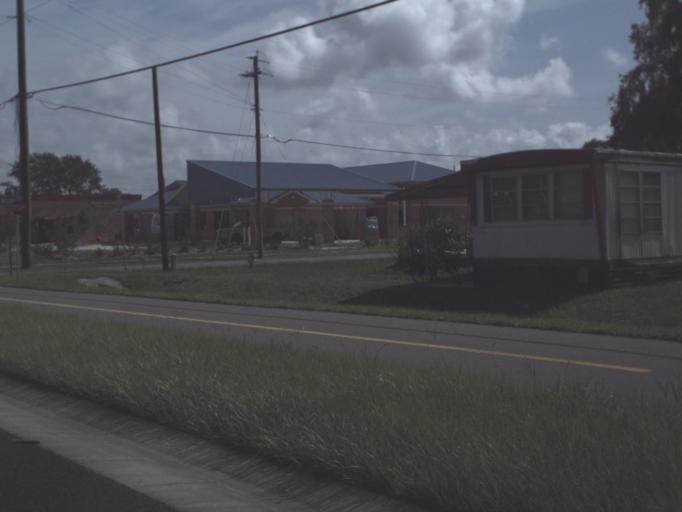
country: US
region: Florida
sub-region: Hillsborough County
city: Riverview
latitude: 27.8532
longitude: -82.3265
